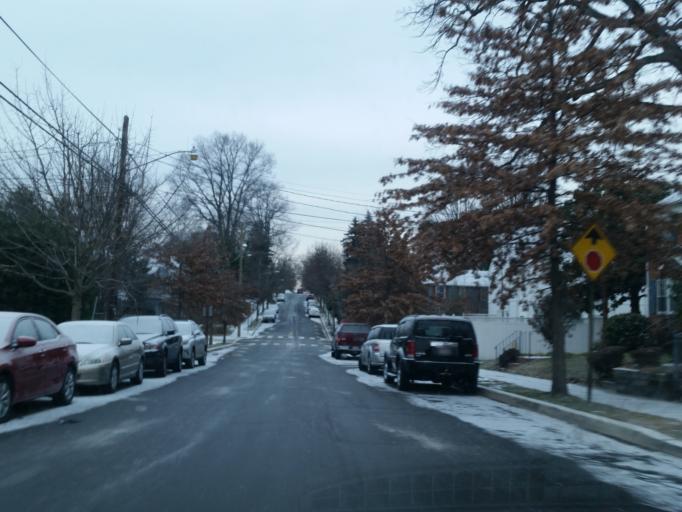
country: US
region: Maryland
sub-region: Montgomery County
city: Silver Spring
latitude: 38.9794
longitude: -77.0270
